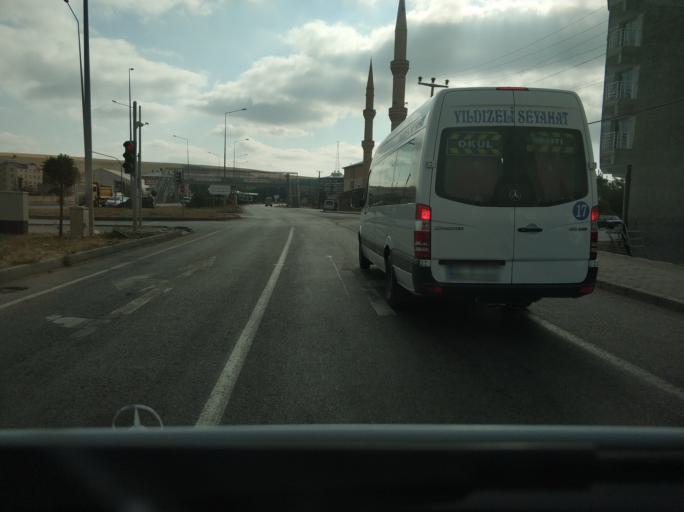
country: TR
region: Sivas
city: Yildizeli
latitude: 39.8715
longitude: 36.5985
